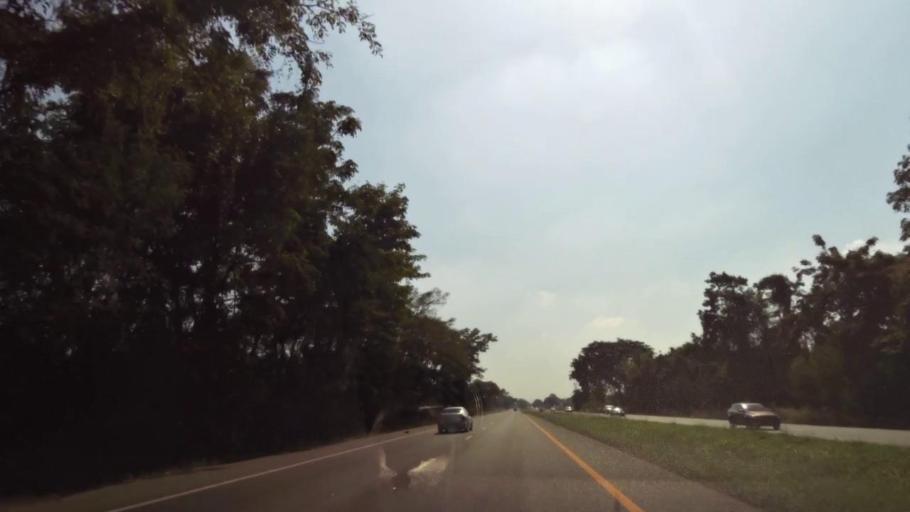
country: TH
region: Phichit
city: Bueng Na Rang
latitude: 16.1994
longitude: 100.1281
